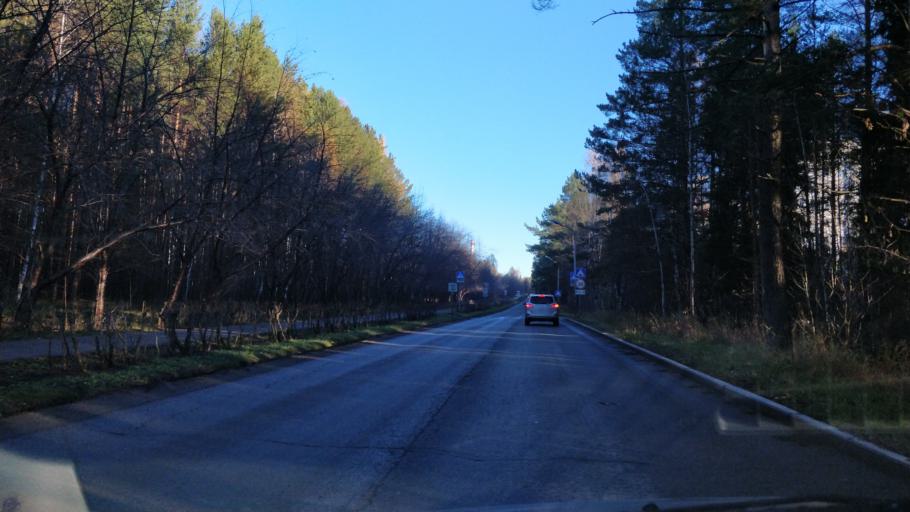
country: RU
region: Perm
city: Perm
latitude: 58.0492
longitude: 56.2133
